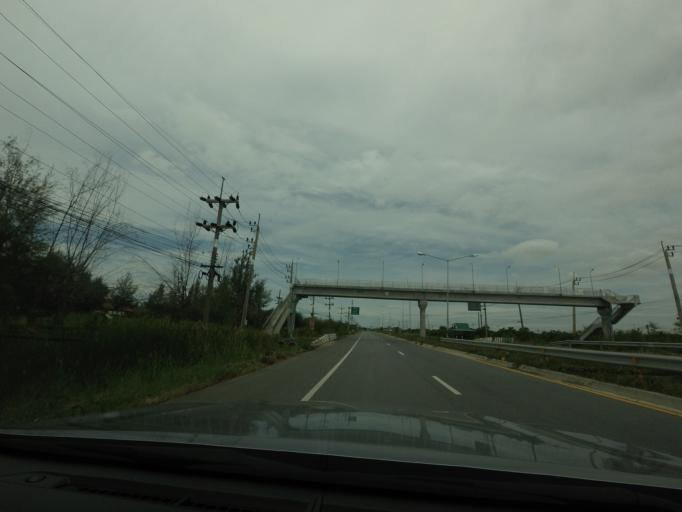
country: TH
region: Songkhla
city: Ranot
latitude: 7.8986
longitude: 100.3404
